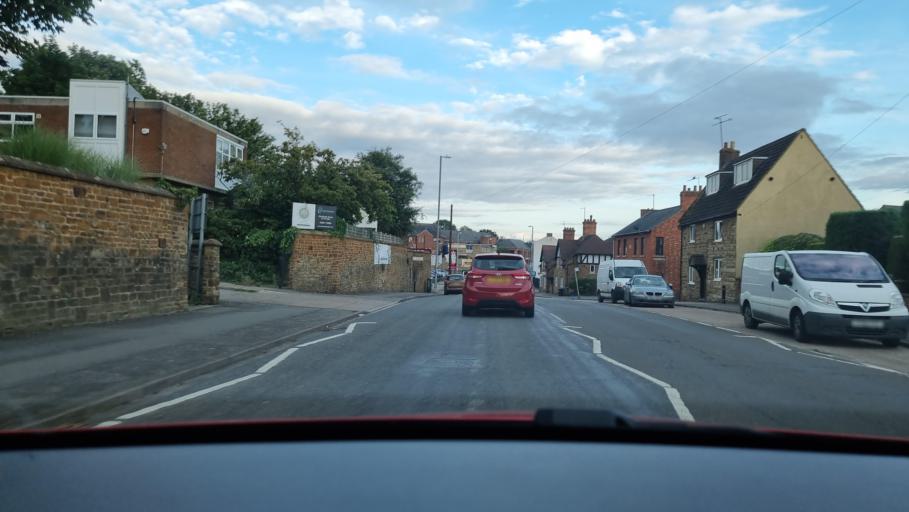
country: GB
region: England
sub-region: Northamptonshire
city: Northampton
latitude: 52.2648
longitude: -0.9027
